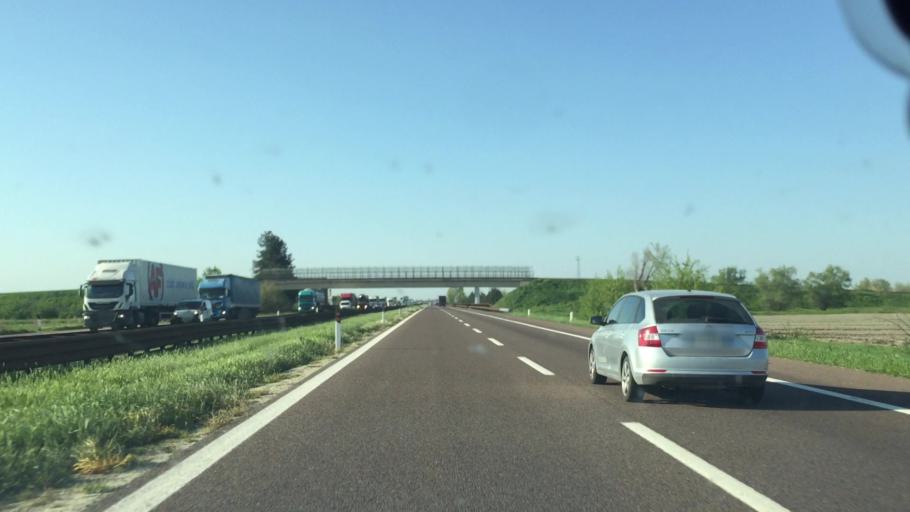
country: IT
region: Emilia-Romagna
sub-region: Provincia di Modena
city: Migliarina
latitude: 44.8354
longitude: 10.8526
